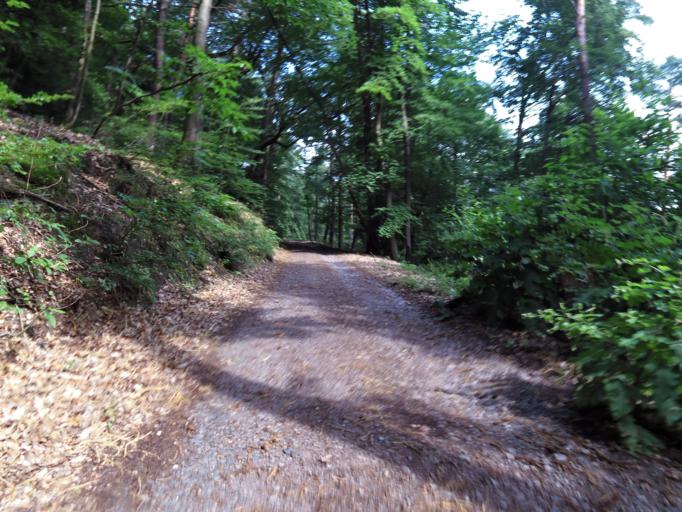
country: DE
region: Rheinland-Pfalz
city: Bad Duerkheim
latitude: 49.4448
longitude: 8.1275
